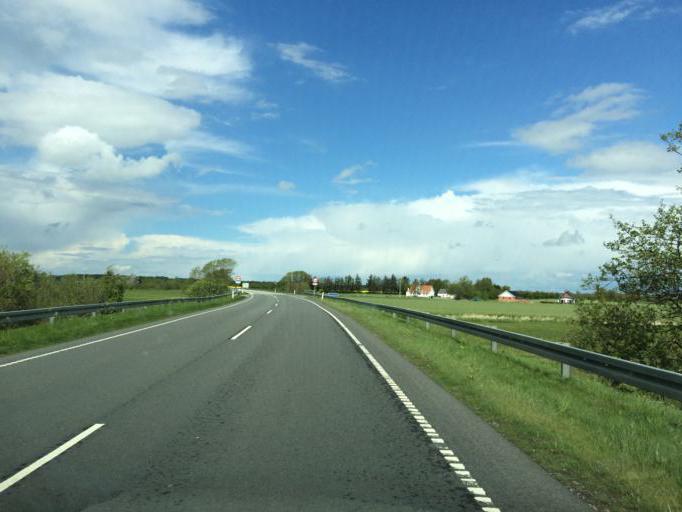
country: DK
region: North Denmark
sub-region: Vesthimmerland Kommune
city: Farso
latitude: 56.6930
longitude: 9.3171
